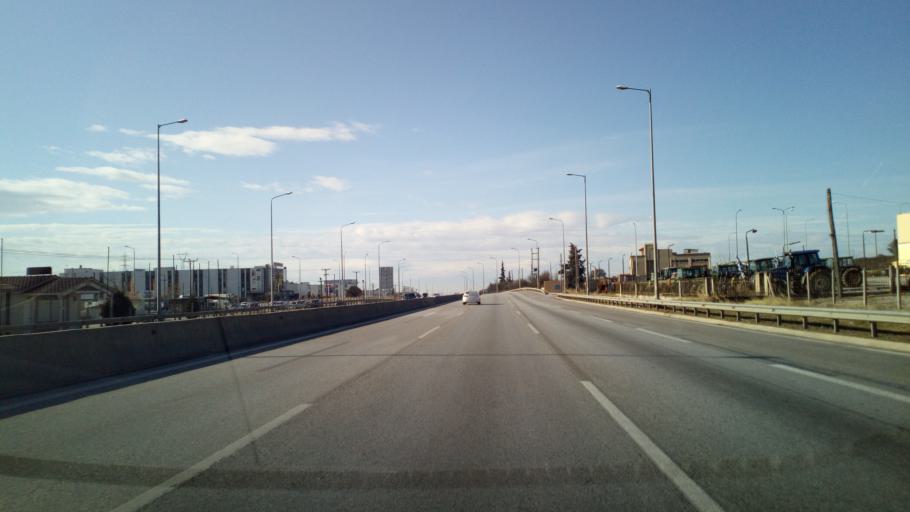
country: GR
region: Central Macedonia
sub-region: Nomos Thessalonikis
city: Liti
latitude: 40.7227
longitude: 22.9757
